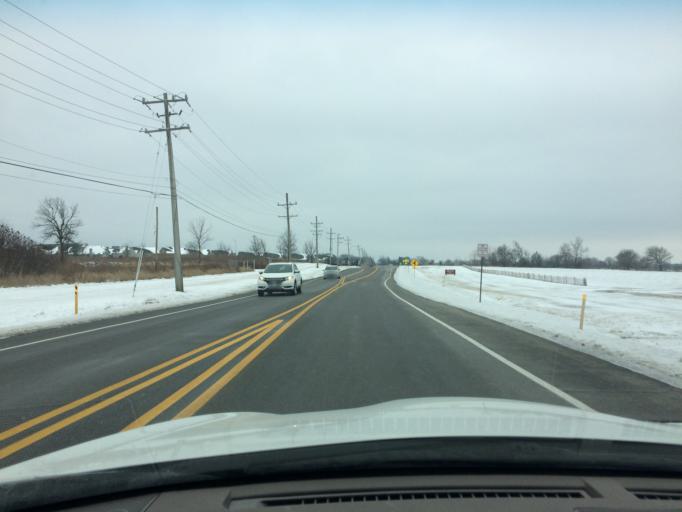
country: US
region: Illinois
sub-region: Kane County
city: Saint Charles
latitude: 41.8999
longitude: -88.3594
